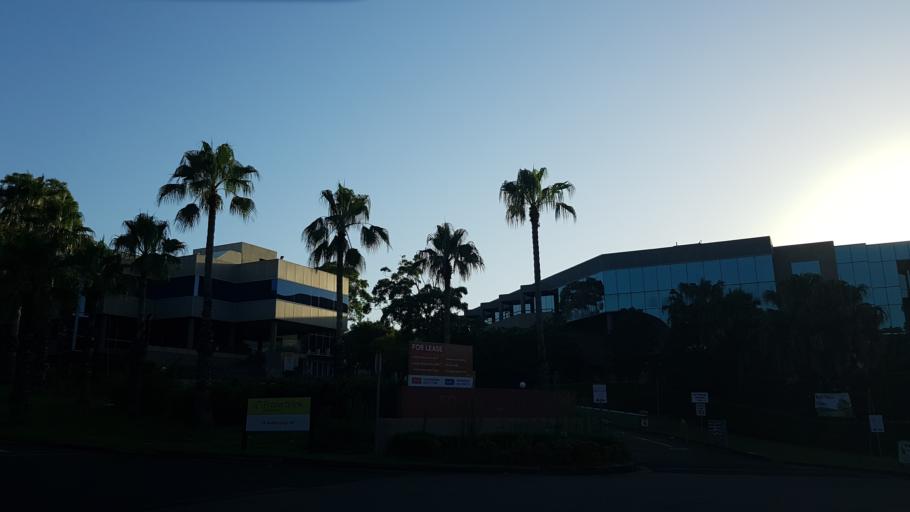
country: AU
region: New South Wales
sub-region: Warringah
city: Allambie Heights
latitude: -33.7541
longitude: 151.2479
